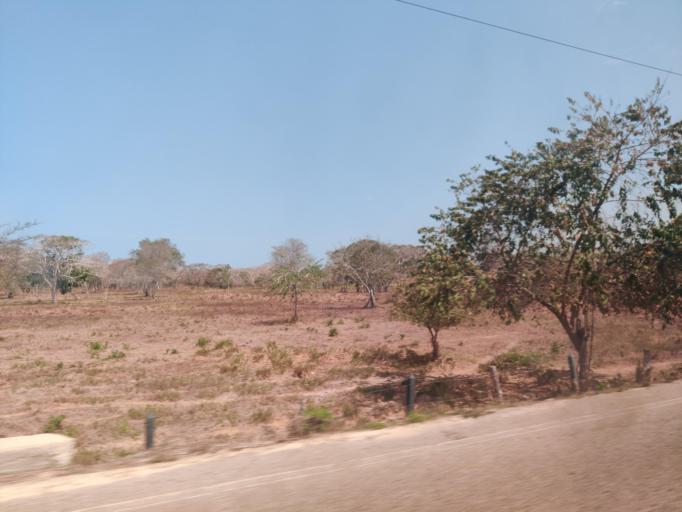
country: CO
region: Bolivar
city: Turbana
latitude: 10.2112
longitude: -75.6042
